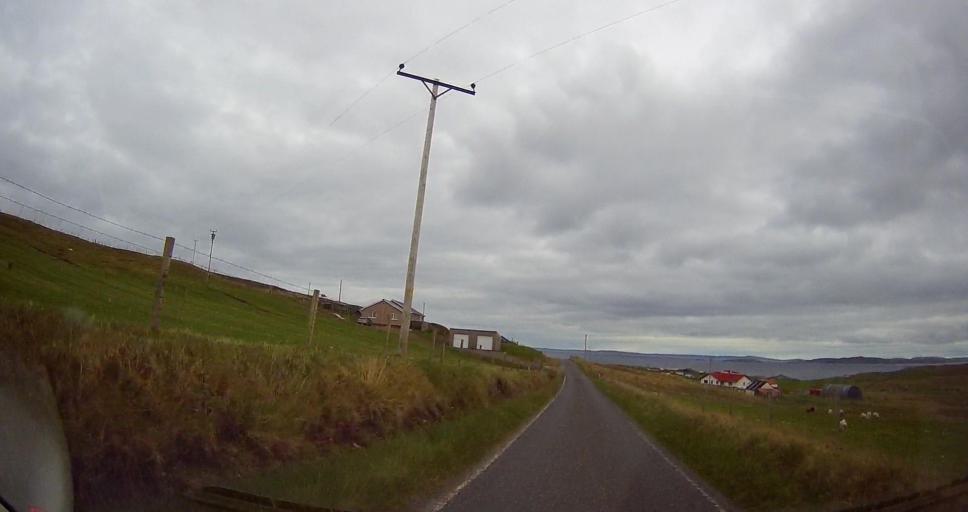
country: GB
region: Scotland
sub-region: Shetland Islands
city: Shetland
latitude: 60.5047
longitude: -1.0597
